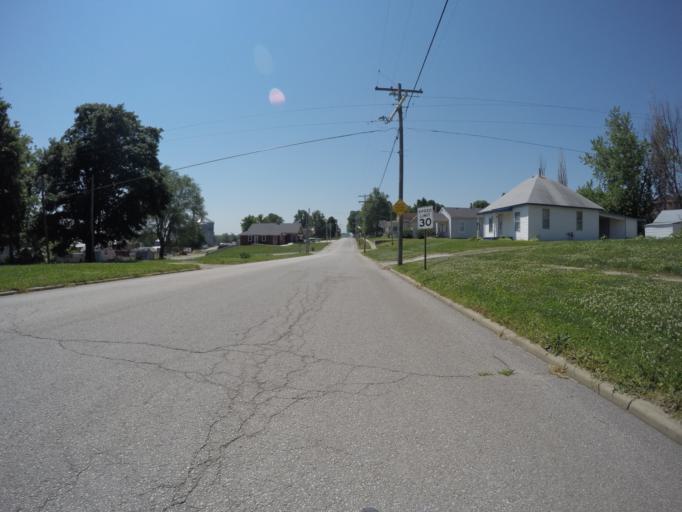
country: US
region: Kansas
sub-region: Doniphan County
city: Highland
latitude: 39.8593
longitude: -95.2652
